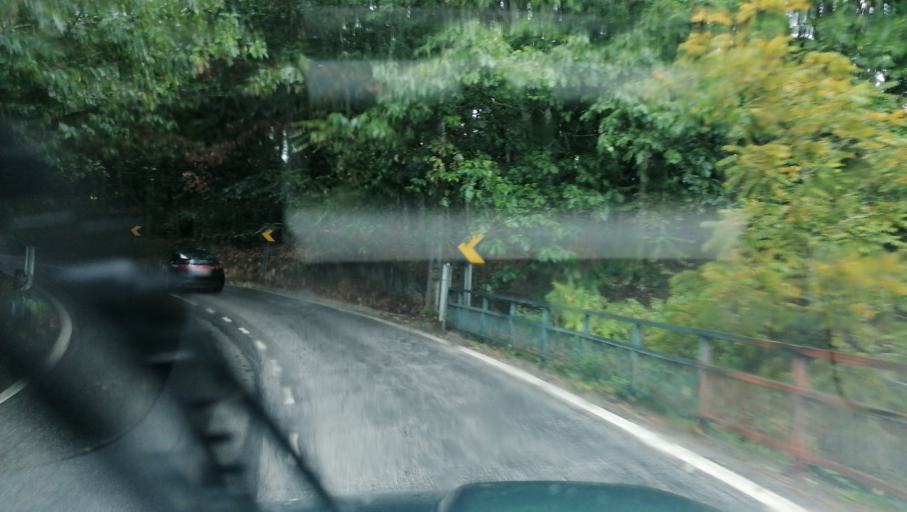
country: PT
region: Braga
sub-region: Cabeceiras de Basto
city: Cabeceiras de Basto
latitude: 41.5006
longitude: -7.9081
